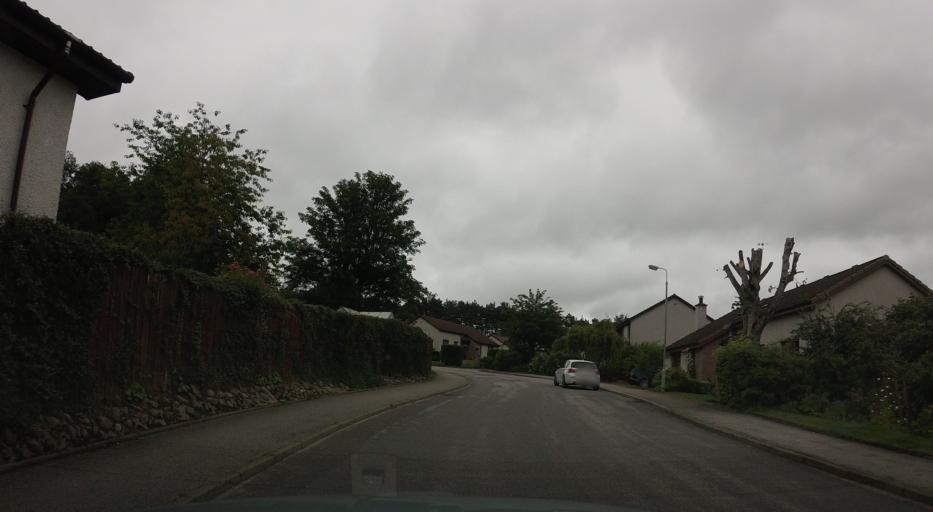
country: GB
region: Scotland
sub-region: Aberdeenshire
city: Banchory
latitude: 57.0581
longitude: -2.4847
